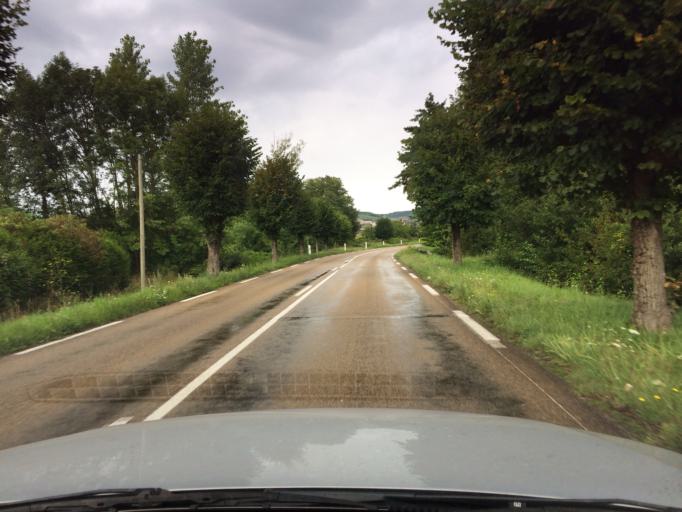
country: FR
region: Bourgogne
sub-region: Departement de l'Yonne
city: Joigny
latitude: 47.9712
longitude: 3.3889
